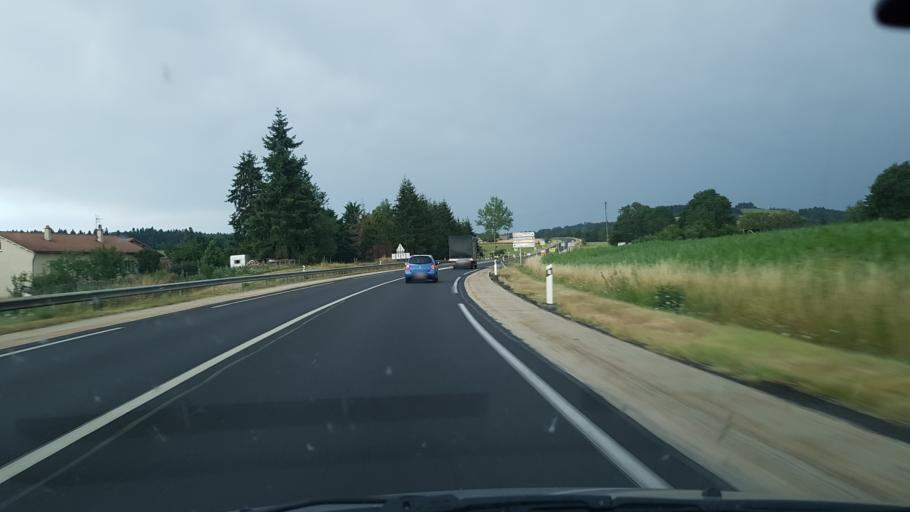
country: FR
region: Auvergne
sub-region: Departement de la Haute-Loire
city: Allegre
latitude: 45.1390
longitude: 3.6291
